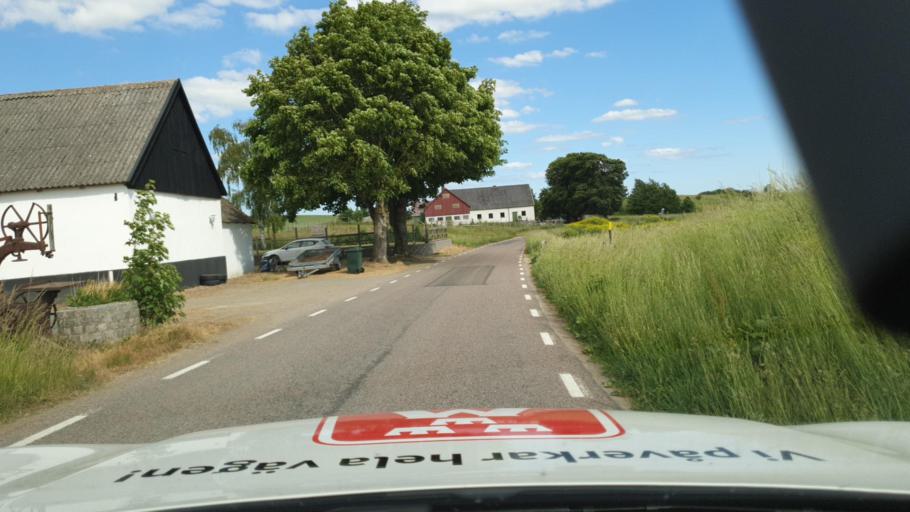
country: SE
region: Skane
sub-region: Ystads Kommun
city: Kopingebro
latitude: 55.4697
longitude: 13.9680
